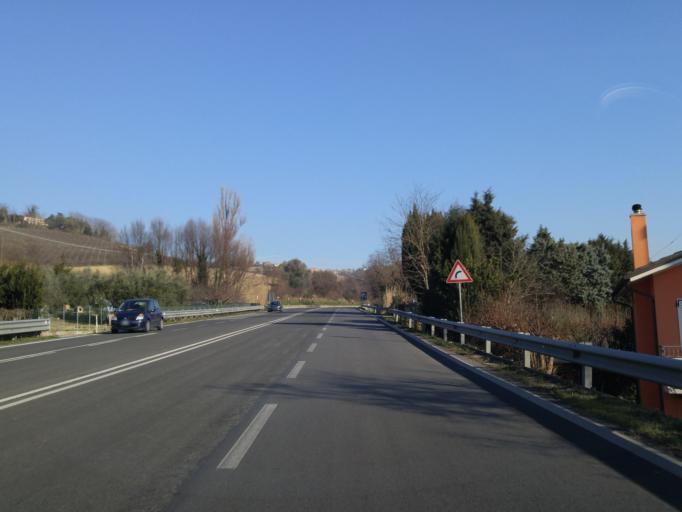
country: IT
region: The Marches
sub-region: Provincia di Pesaro e Urbino
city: Gradara
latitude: 43.9479
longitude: 12.8076
